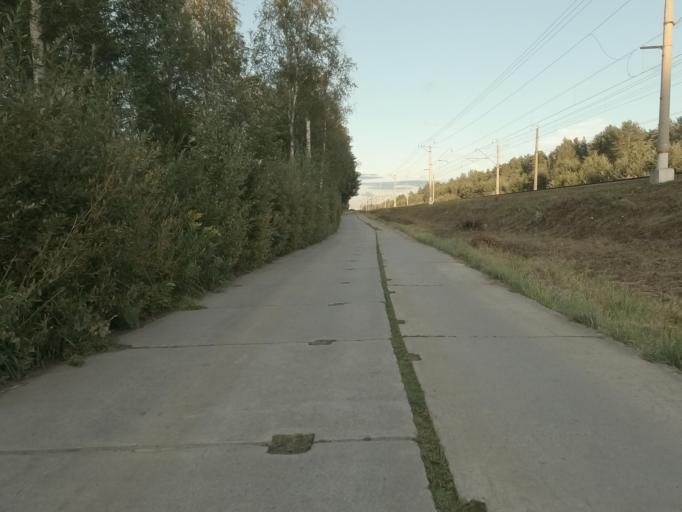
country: RU
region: Leningrad
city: Mga
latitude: 59.7624
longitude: 30.9982
